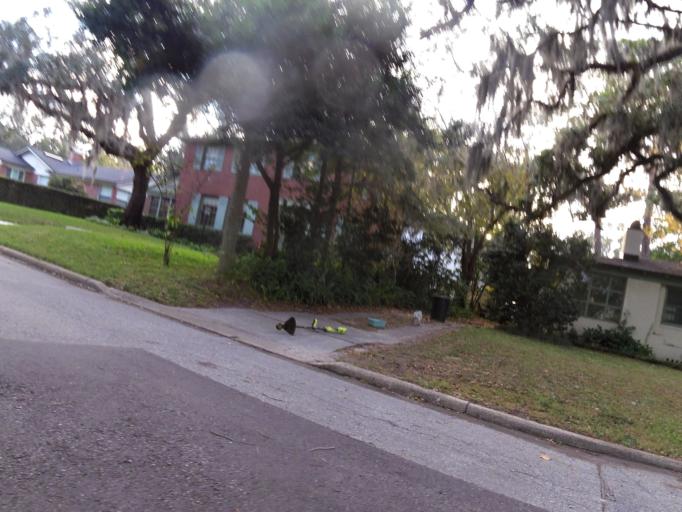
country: US
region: Florida
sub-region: Duval County
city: Jacksonville
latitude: 30.3096
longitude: -81.6370
